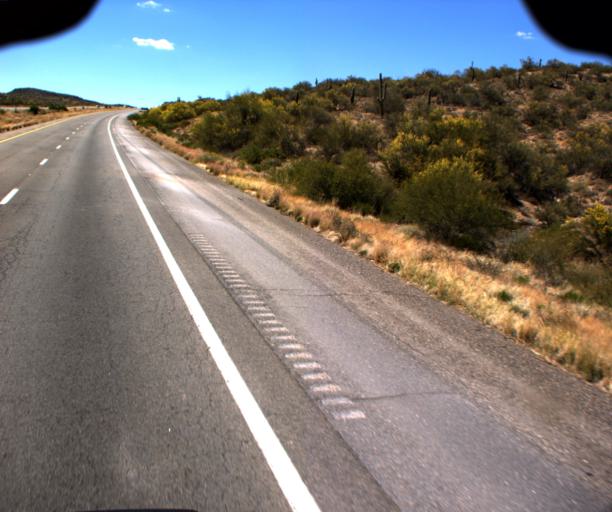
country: US
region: Arizona
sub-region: Yavapai County
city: Bagdad
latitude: 34.4287
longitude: -113.2477
